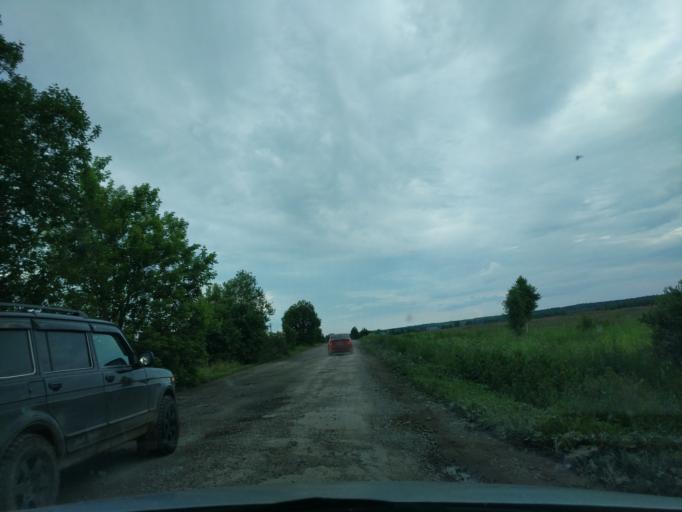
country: RU
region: Kaluga
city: Myatlevo
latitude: 54.7889
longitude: 35.7349
